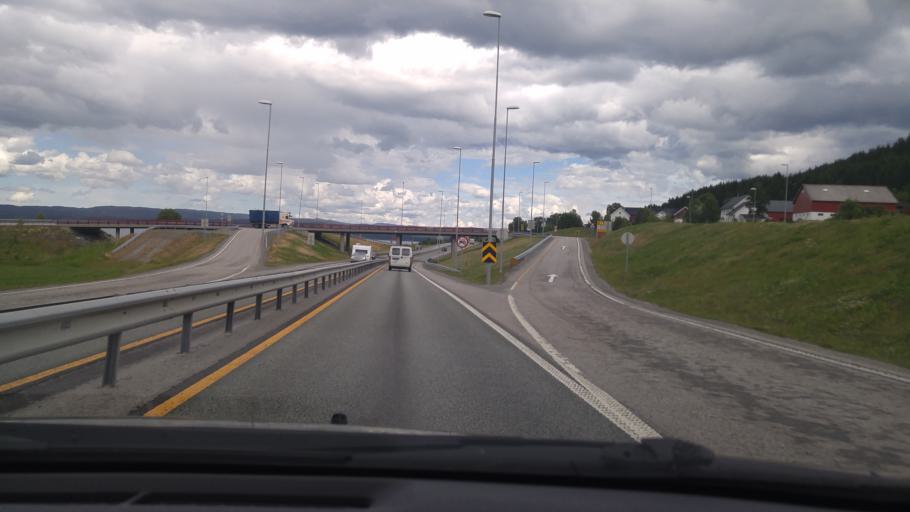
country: NO
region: Nord-Trondelag
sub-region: Steinkjer
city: Steinkjer
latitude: 63.9677
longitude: 11.4157
